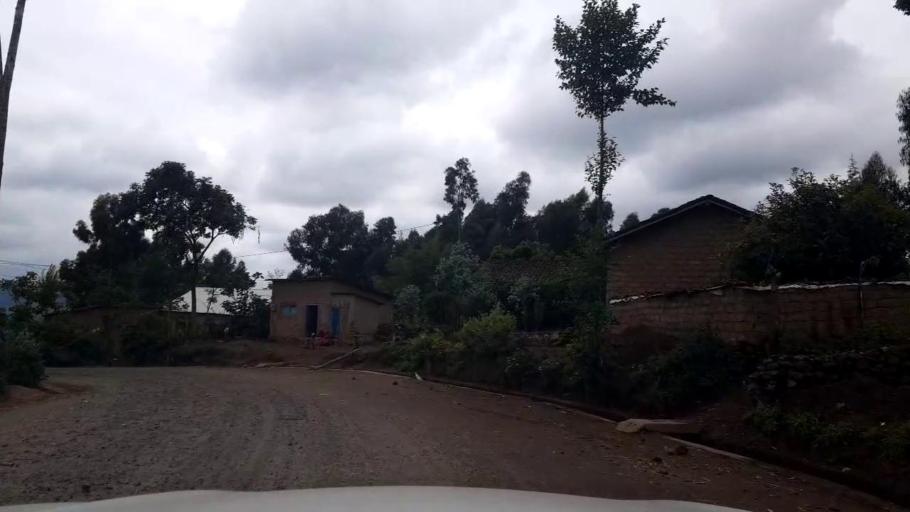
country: RW
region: Northern Province
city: Musanze
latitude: -1.5431
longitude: 29.5308
